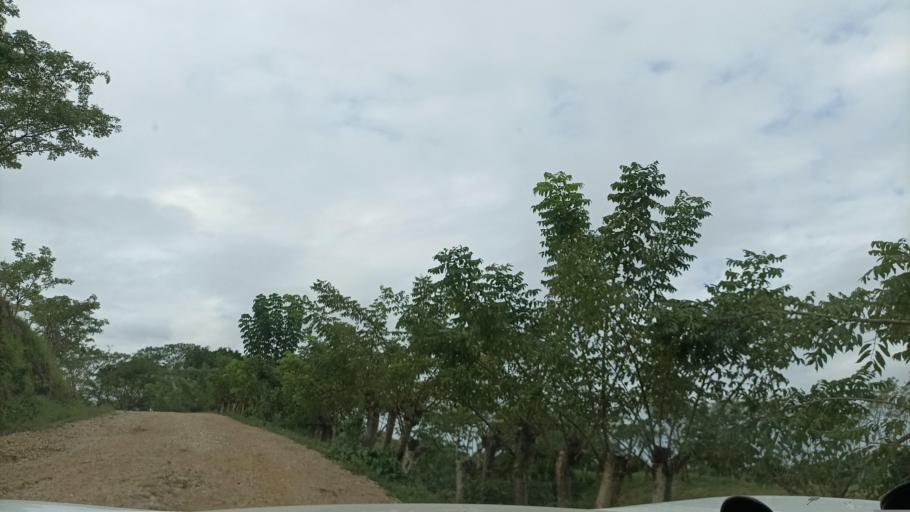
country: MX
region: Veracruz
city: Hidalgotitlan
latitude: 17.5946
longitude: -94.4208
